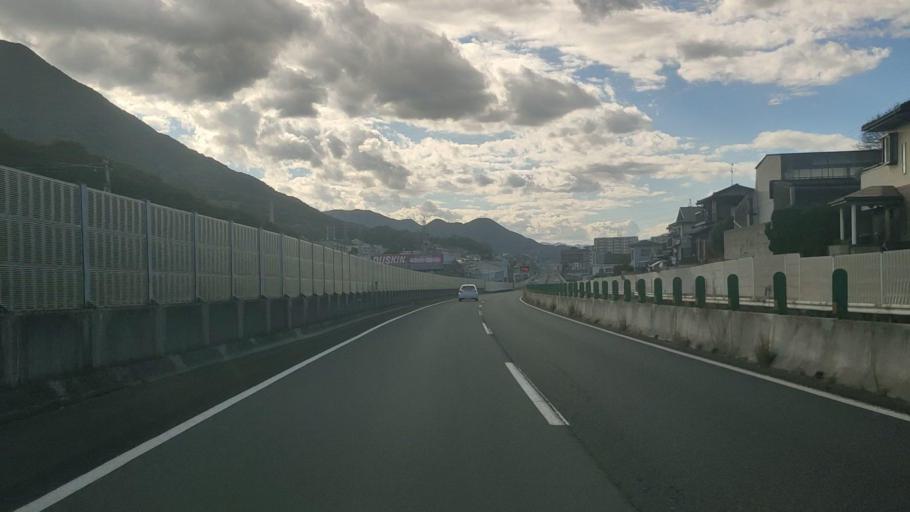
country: JP
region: Yamaguchi
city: Shimonoseki
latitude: 33.9101
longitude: 130.9562
